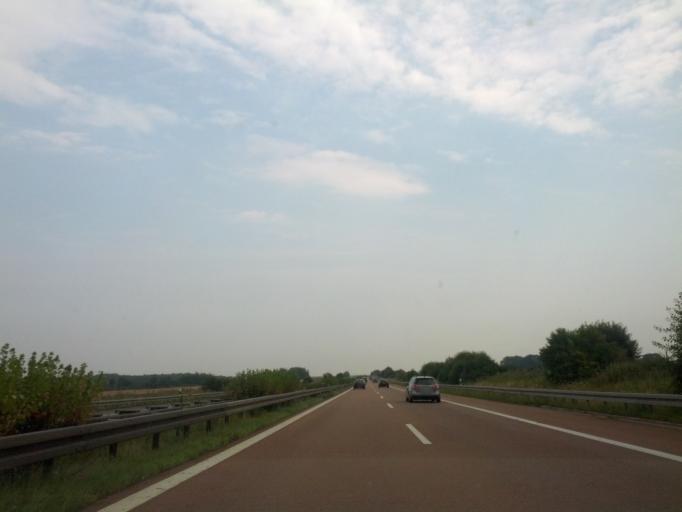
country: DE
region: Mecklenburg-Vorpommern
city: Dummerstorf
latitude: 54.0258
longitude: 12.2588
